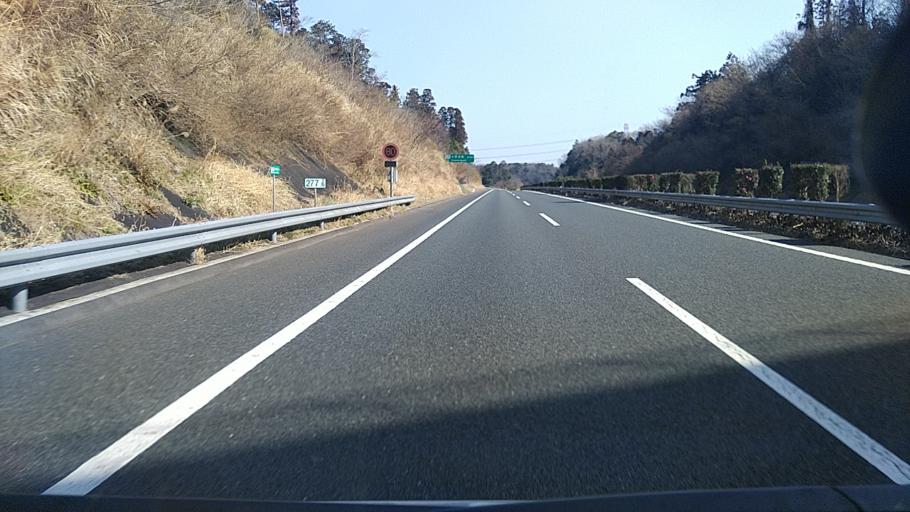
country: JP
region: Chiba
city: Kisarazu
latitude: 35.3576
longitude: 140.0228
